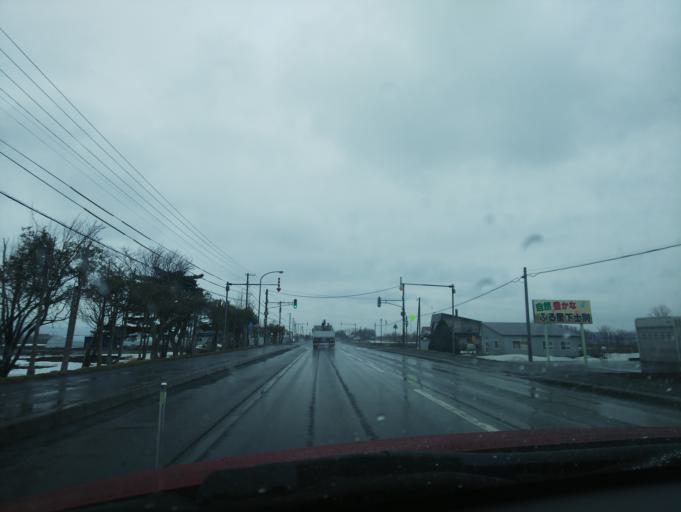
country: JP
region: Hokkaido
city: Nayoro
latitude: 44.2118
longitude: 142.3949
